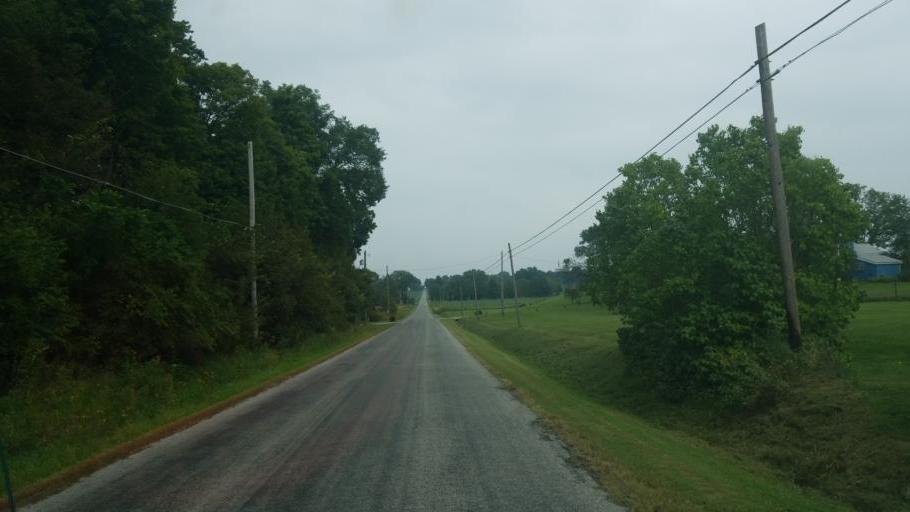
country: US
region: Ohio
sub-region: Wayne County
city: Creston
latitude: 40.9599
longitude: -81.9154
